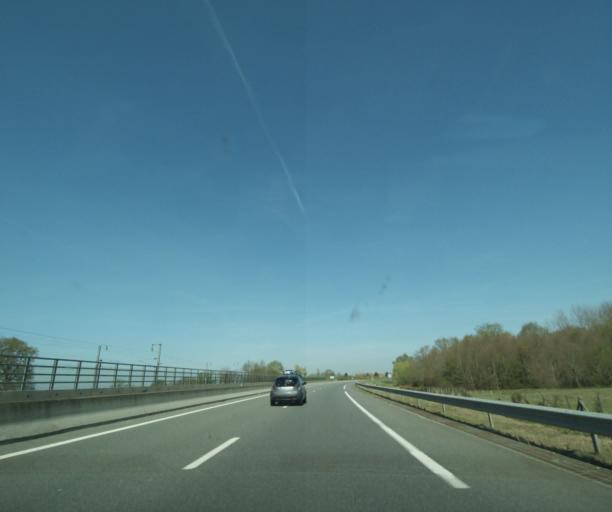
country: FR
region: Auvergne
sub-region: Departement de l'Allier
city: Trevol
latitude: 46.6125
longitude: 3.2911
